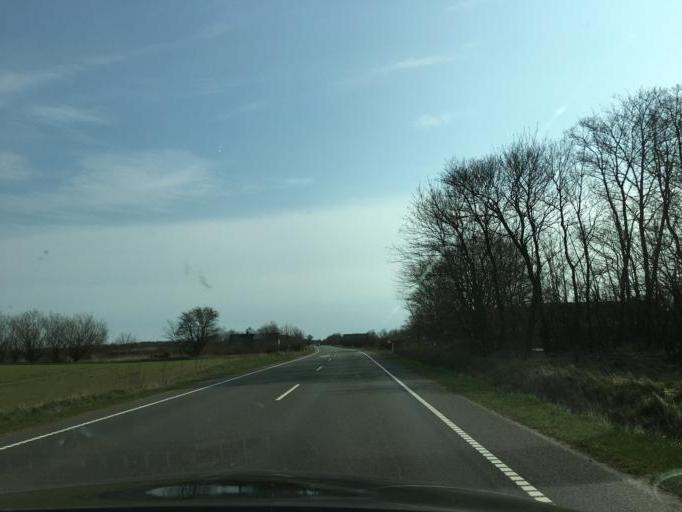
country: DK
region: South Denmark
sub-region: Vejen Kommune
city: Vejen
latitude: 55.4734
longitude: 9.2069
